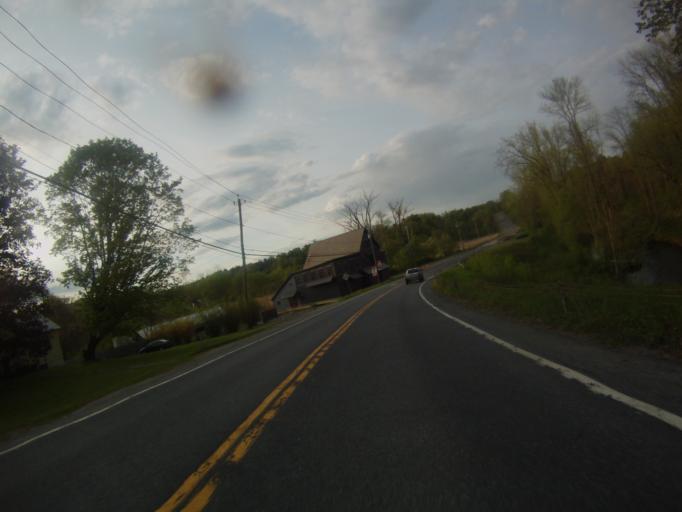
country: US
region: New York
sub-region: Essex County
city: Port Henry
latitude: 43.9548
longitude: -73.4330
